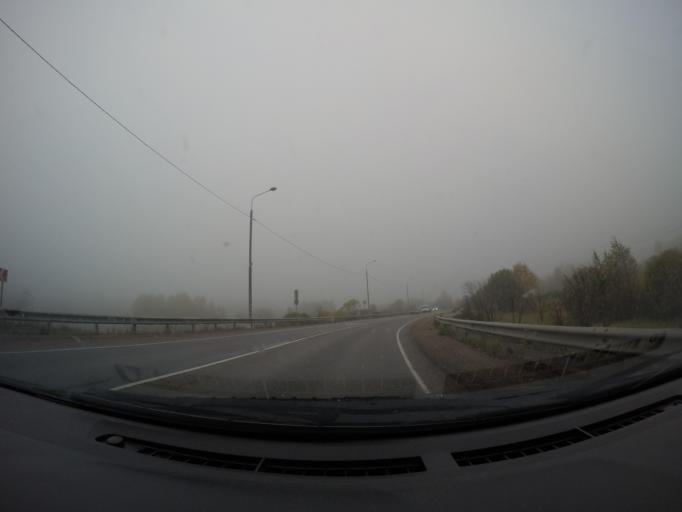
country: RU
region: Moskovskaya
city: Ruza
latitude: 55.7288
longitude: 36.3086
